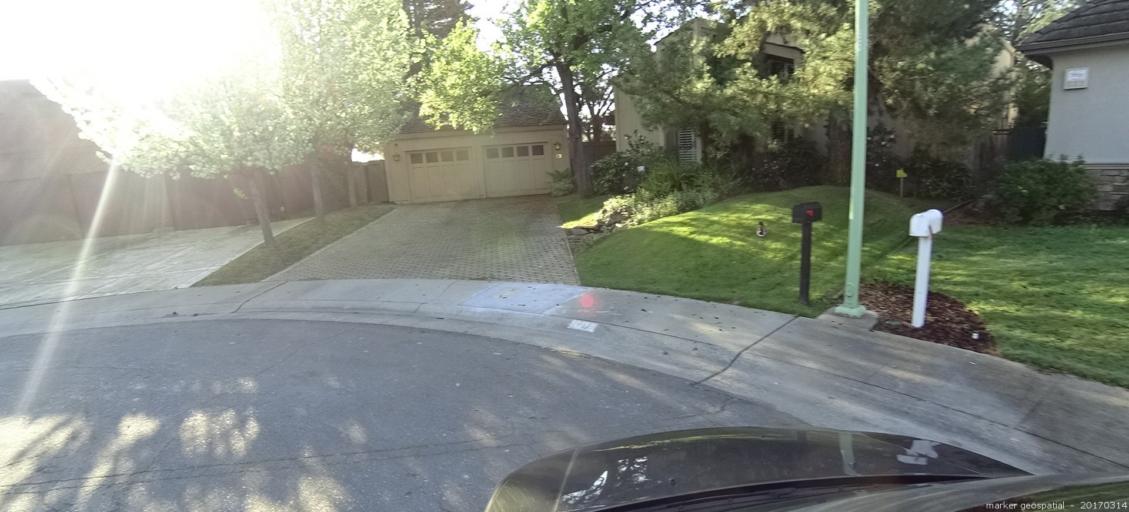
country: US
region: California
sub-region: Yolo County
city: West Sacramento
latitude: 38.5091
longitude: -121.5388
